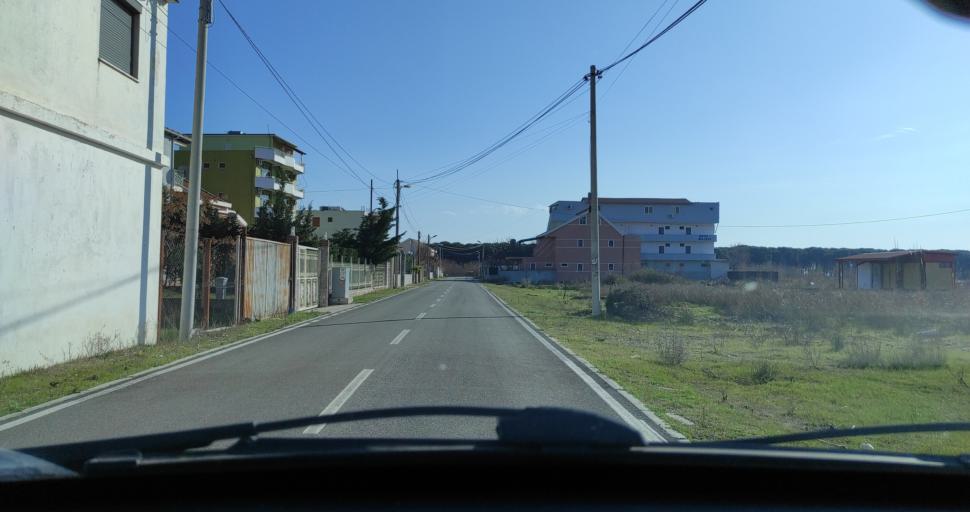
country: AL
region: Shkoder
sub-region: Rrethi i Shkodres
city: Velipoje
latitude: 41.8641
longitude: 19.4353
